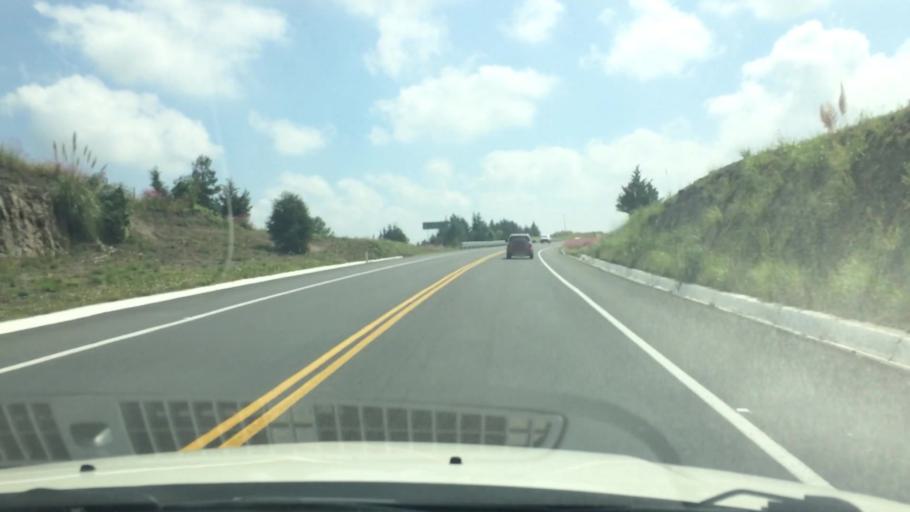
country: MX
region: Mexico
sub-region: Villa Victoria
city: Colonia Doctor Gustavo Baz
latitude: 19.3773
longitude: -99.8829
